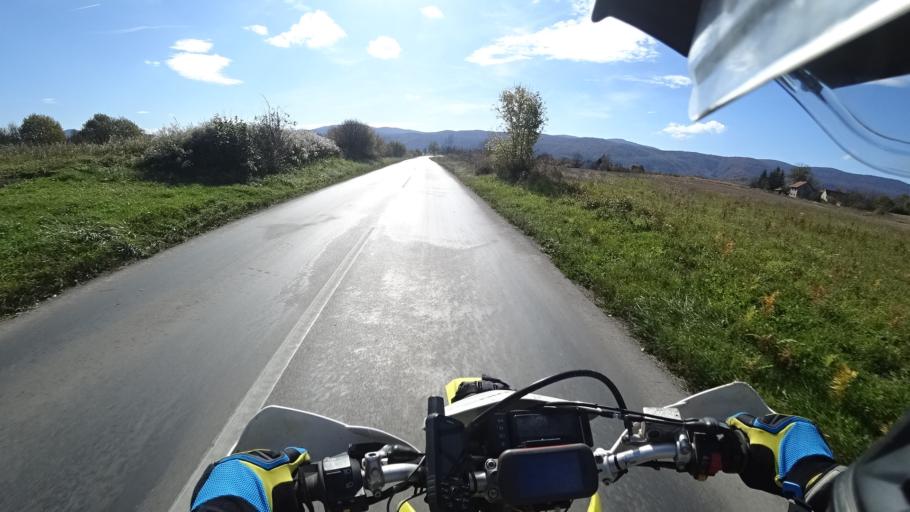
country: HR
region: Karlovacka
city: Plaski
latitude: 45.1059
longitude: 15.3594
